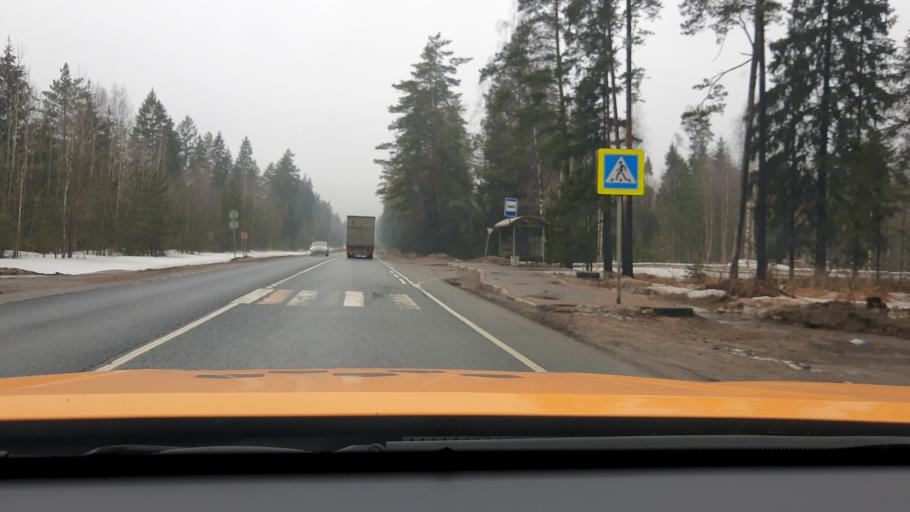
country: RU
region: Moskovskaya
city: Chernogolovka
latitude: 55.9885
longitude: 38.3317
